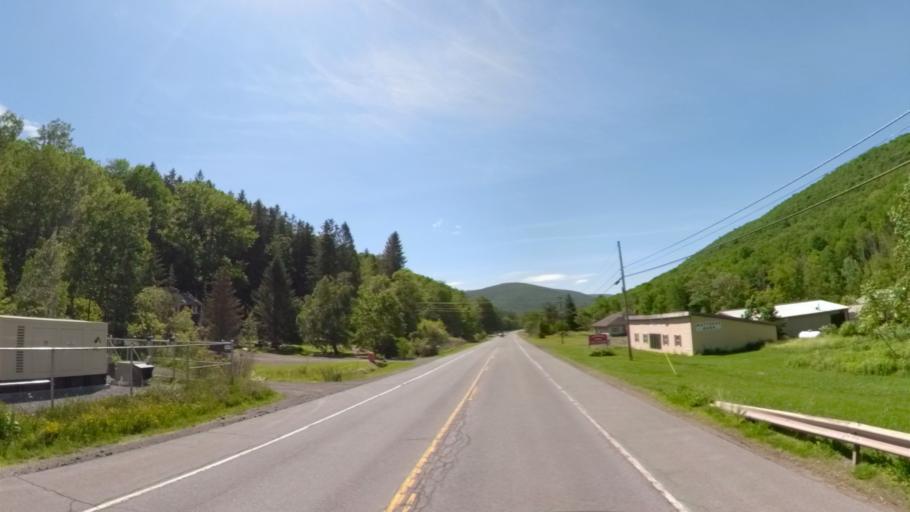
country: US
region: New York
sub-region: Ulster County
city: Shokan
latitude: 42.1198
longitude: -74.4592
